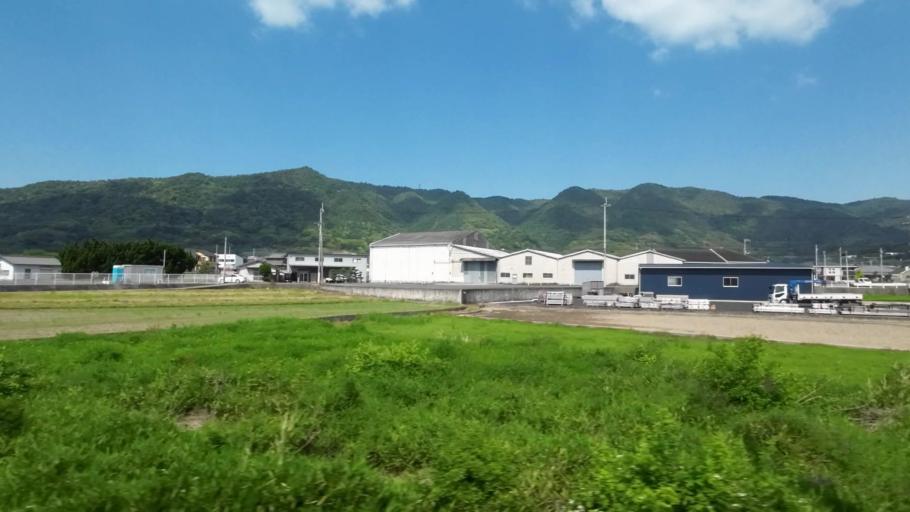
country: JP
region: Kagawa
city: Kan'onjicho
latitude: 34.1618
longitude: 133.6893
